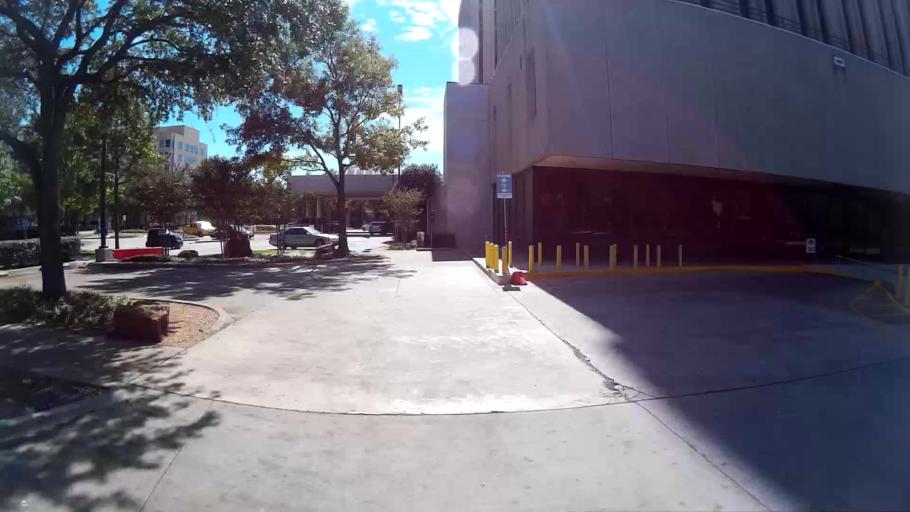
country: US
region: Texas
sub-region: Dallas County
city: Dallas
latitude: 32.7914
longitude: -96.7797
